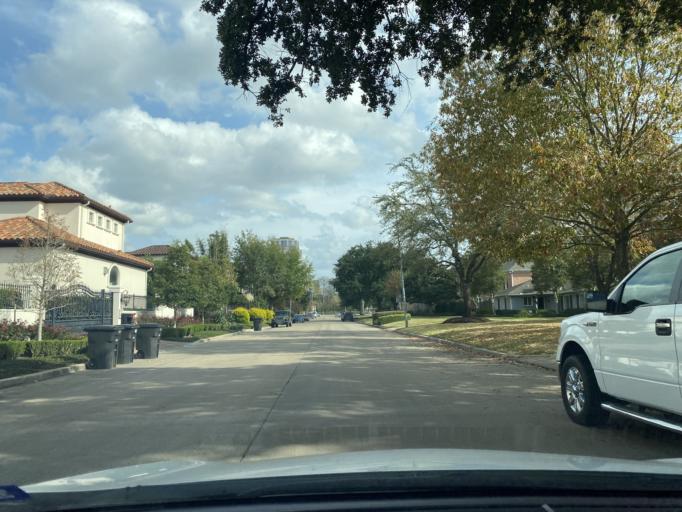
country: US
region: Texas
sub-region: Harris County
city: Hunters Creek Village
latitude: 29.7557
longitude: -95.4657
